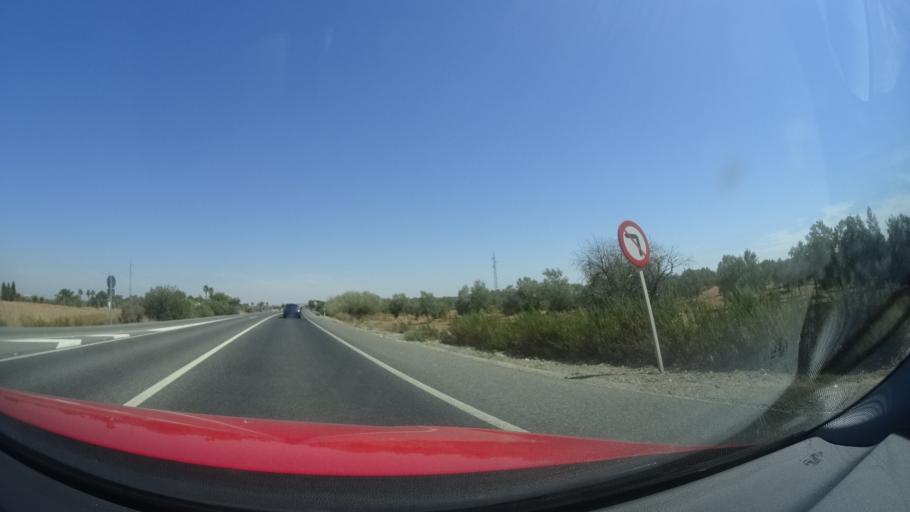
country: ES
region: Andalusia
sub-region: Provincia de Sevilla
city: Las Cabezas de San Juan
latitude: 36.9107
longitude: -5.9647
